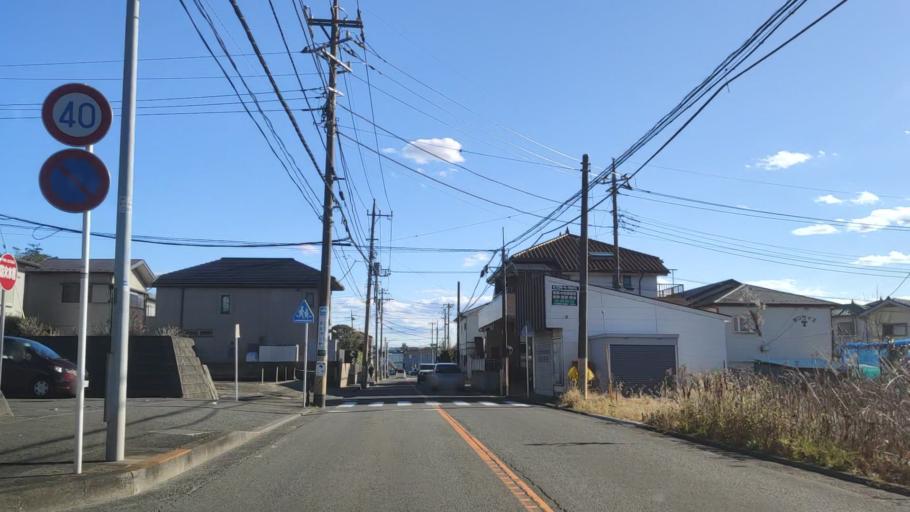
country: JP
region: Tokyo
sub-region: Machida-shi
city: Machida
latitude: 35.5234
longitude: 139.5341
